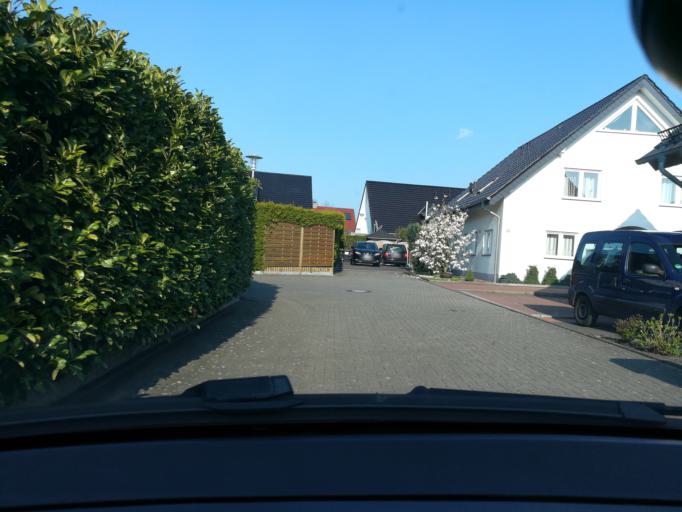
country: DE
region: North Rhine-Westphalia
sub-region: Regierungsbezirk Detmold
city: Oerlinghausen
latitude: 51.9326
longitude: 8.6023
